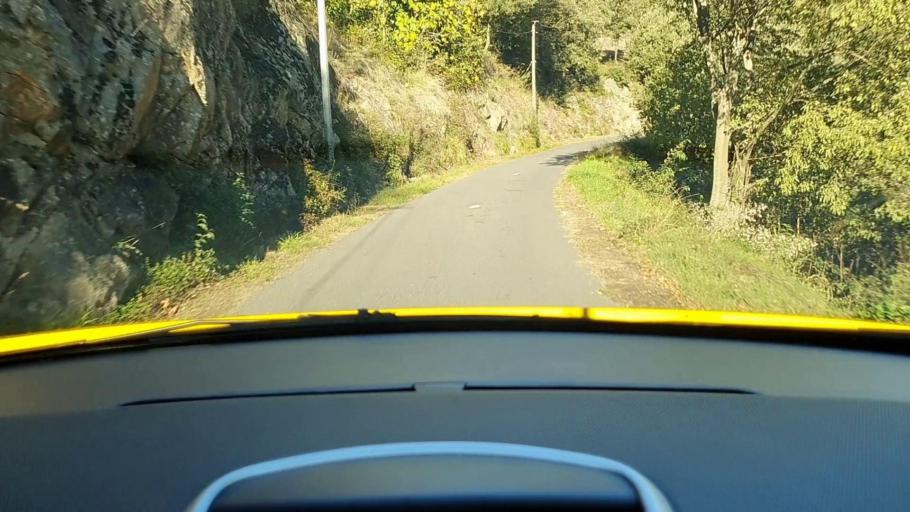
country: FR
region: Languedoc-Roussillon
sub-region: Departement du Gard
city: Sumene
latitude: 44.0262
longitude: 3.7591
